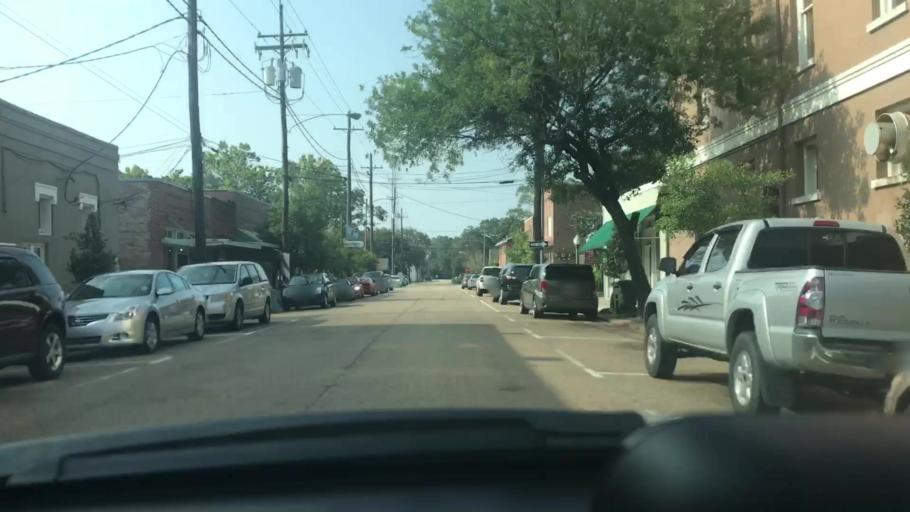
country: US
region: Louisiana
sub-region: Tangipahoa Parish
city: Hammond
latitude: 30.5045
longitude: -90.4597
